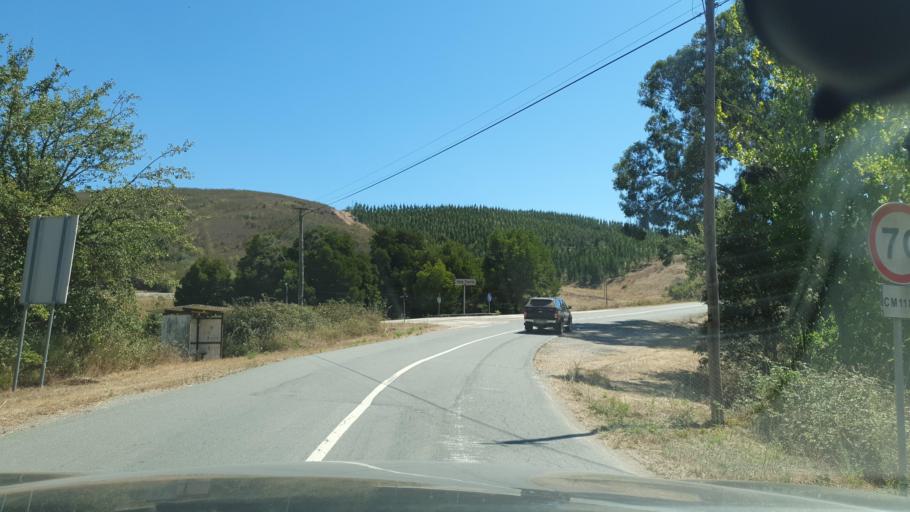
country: PT
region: Faro
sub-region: Monchique
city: Monchique
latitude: 37.4329
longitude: -8.5302
